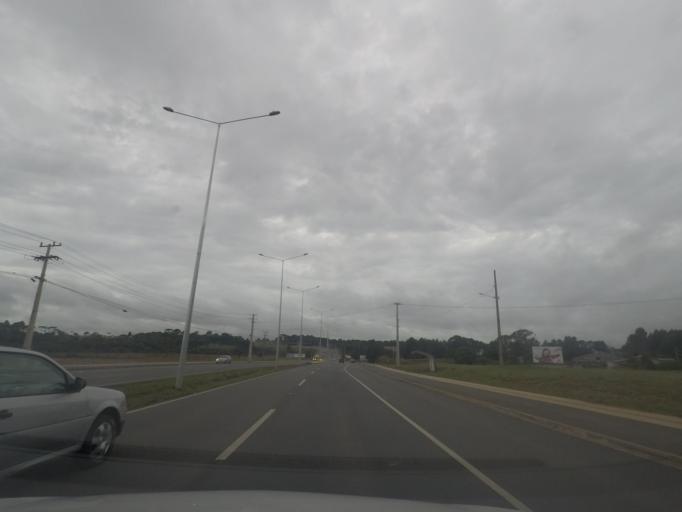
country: BR
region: Parana
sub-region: Piraquara
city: Piraquara
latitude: -25.4614
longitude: -49.0875
